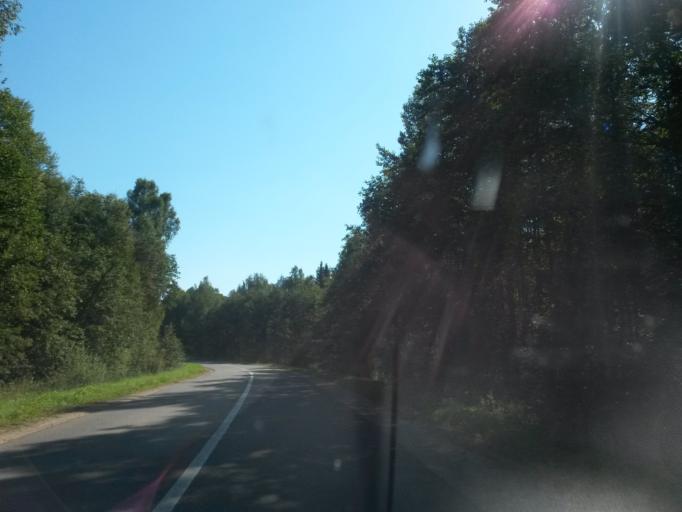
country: RU
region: Jaroslavl
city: Gavrilov-Yam
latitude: 57.3001
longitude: 40.0403
